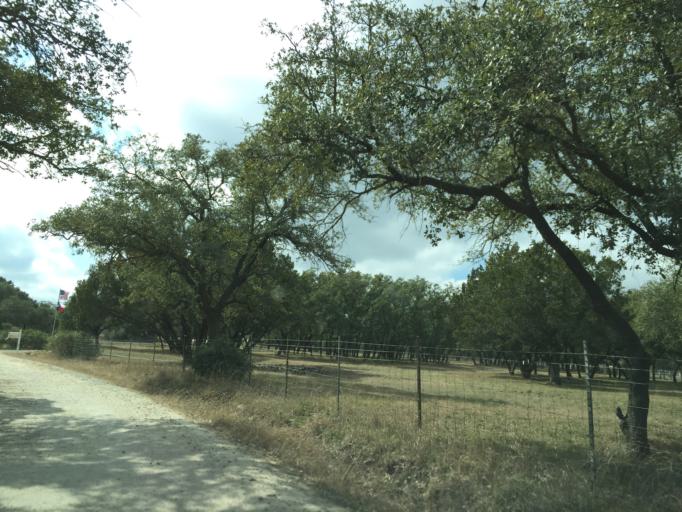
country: US
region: Texas
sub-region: Travis County
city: Briarcliff
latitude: 30.3832
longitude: -98.0954
